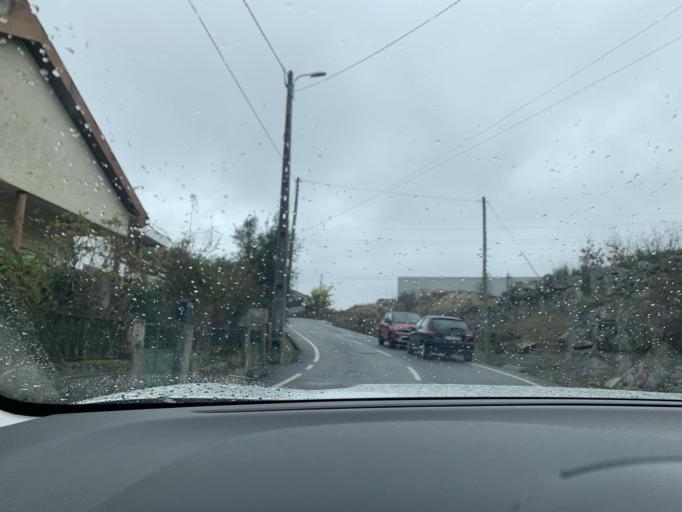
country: PT
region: Viseu
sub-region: Mangualde
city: Mangualde
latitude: 40.6014
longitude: -7.7849
